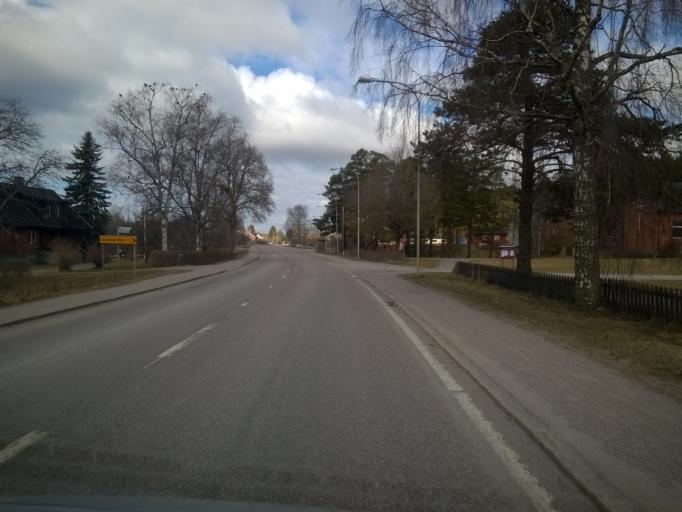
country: SE
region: Uppsala
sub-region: Tierps Kommun
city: Tierp
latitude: 60.2254
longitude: 17.4664
